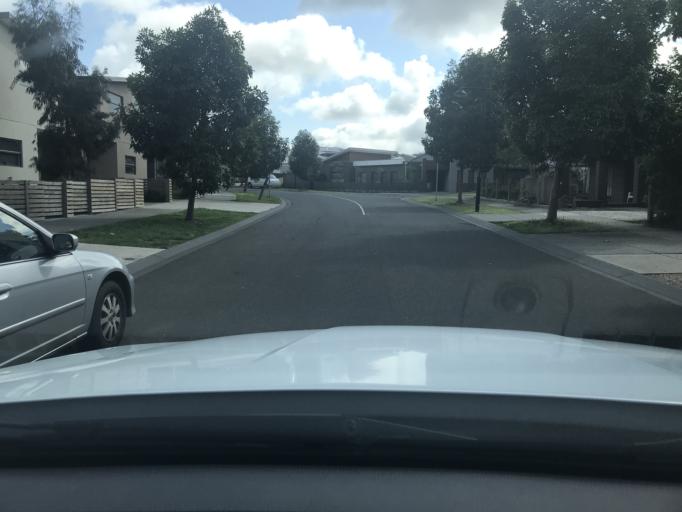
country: AU
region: Victoria
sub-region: Hume
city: Craigieburn
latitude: -37.5791
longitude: 144.9300
